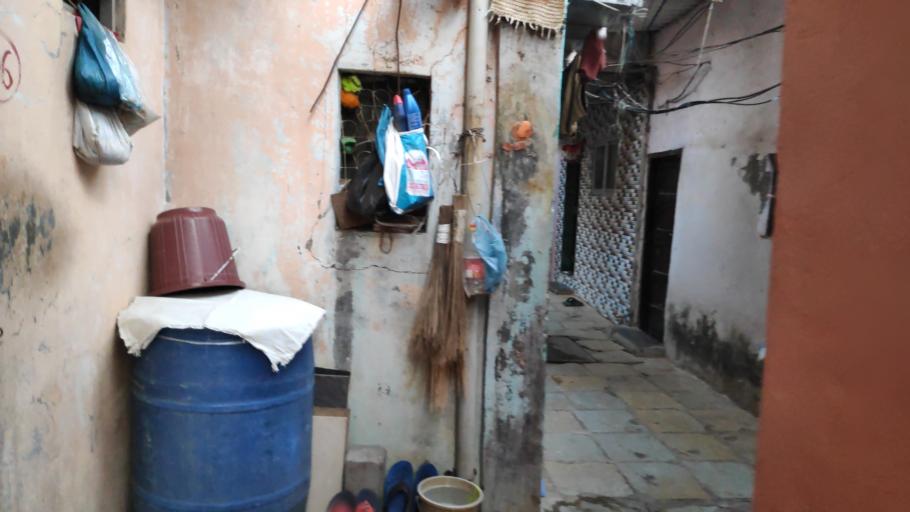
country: IN
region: Maharashtra
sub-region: Mumbai Suburban
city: Mumbai
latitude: 19.0765
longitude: 72.8482
